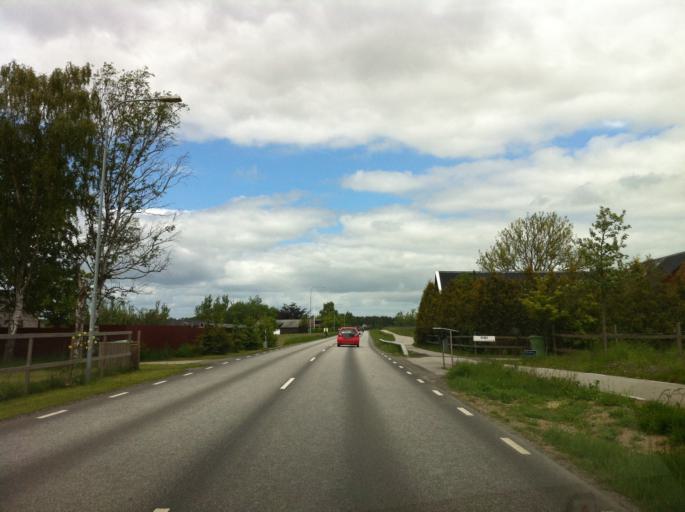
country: SE
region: Skane
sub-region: Kavlinge Kommun
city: Loddekopinge
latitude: 55.7888
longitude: 13.0012
